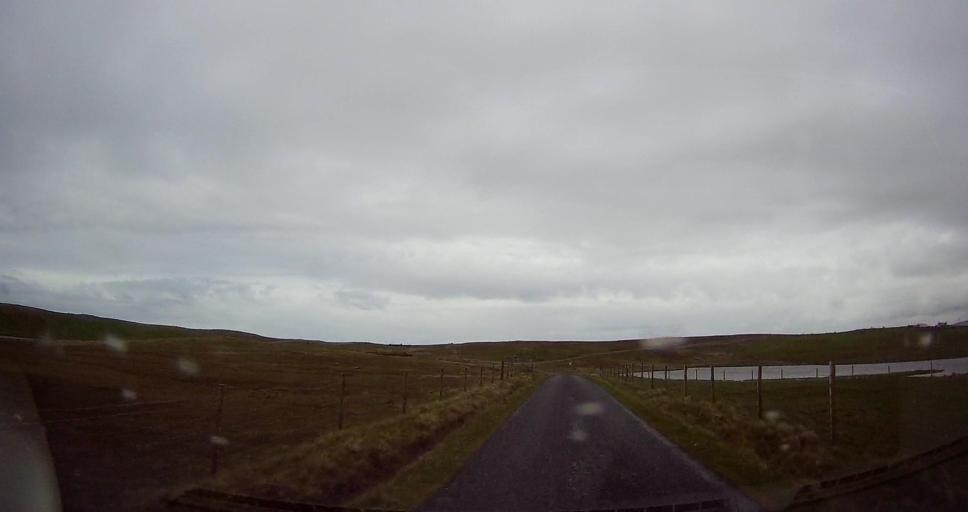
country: GB
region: Scotland
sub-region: Shetland Islands
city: Lerwick
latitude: 60.4826
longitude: -1.6082
